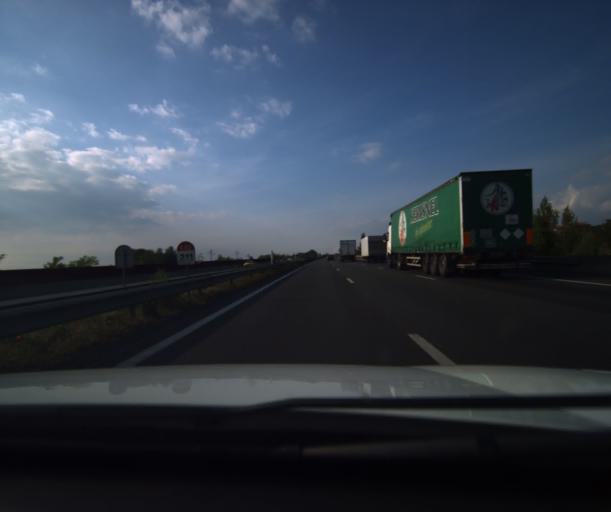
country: FR
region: Midi-Pyrenees
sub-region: Departement de la Haute-Garonne
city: Bouloc
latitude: 43.7750
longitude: 1.3837
